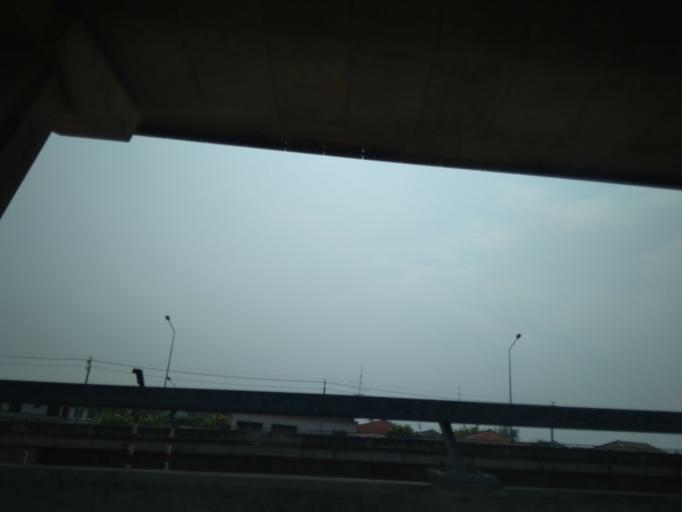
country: TH
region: Bangkok
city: Taling Chan
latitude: 13.7953
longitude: 100.4330
